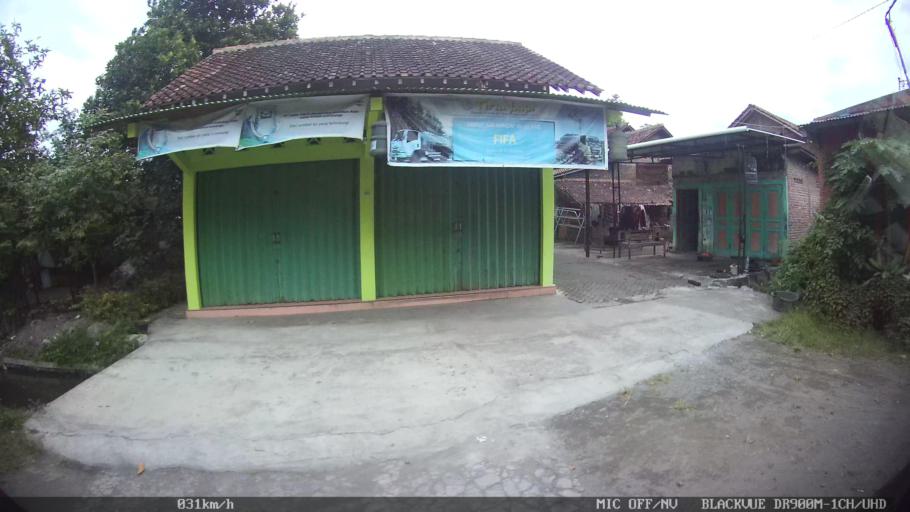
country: ID
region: Daerah Istimewa Yogyakarta
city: Depok
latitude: -7.8300
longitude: 110.4233
